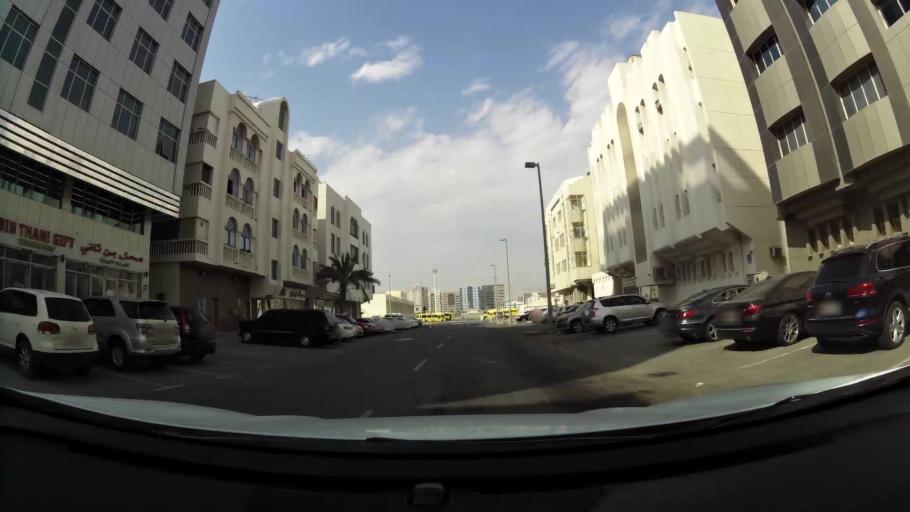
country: AE
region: Abu Dhabi
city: Abu Dhabi
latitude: 24.3281
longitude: 54.5324
